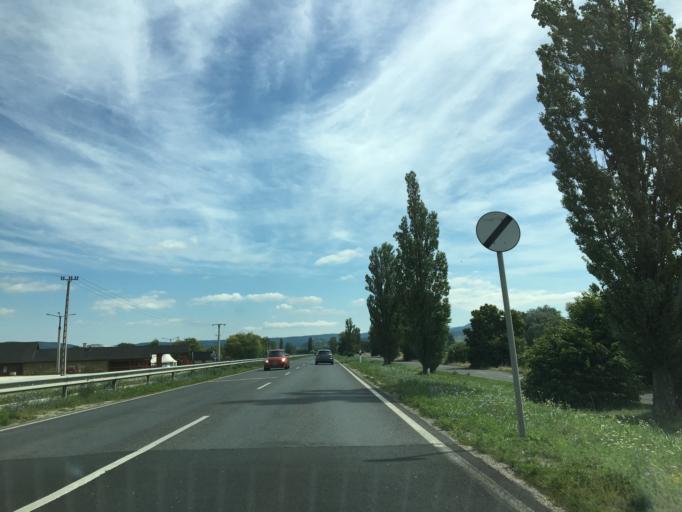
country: HU
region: Komarom-Esztergom
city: Tat
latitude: 47.7468
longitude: 18.6762
